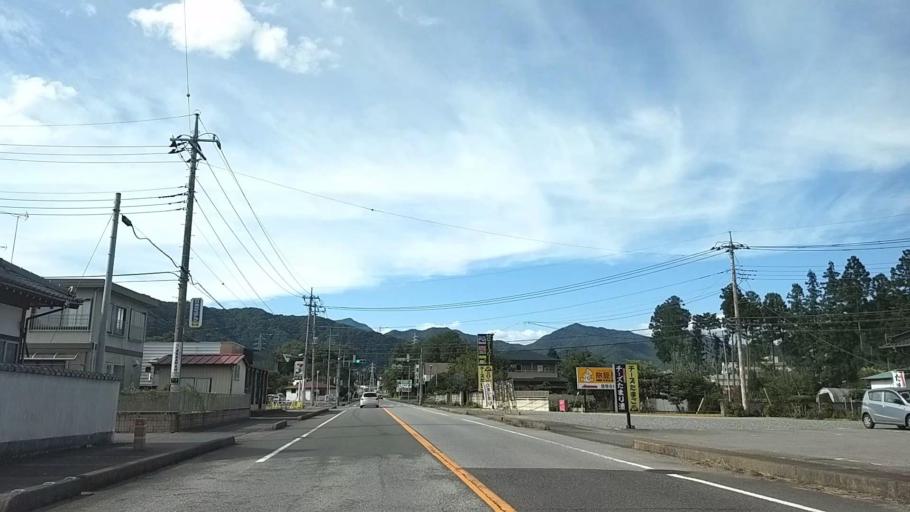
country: JP
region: Tochigi
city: Imaichi
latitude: 36.7795
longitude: 139.7057
